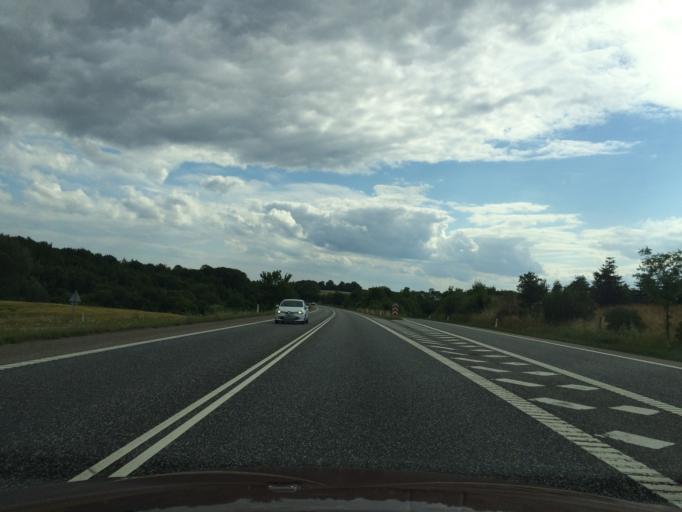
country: DK
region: Central Jutland
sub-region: Syddjurs Kommune
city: Hornslet
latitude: 56.2927
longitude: 10.3342
